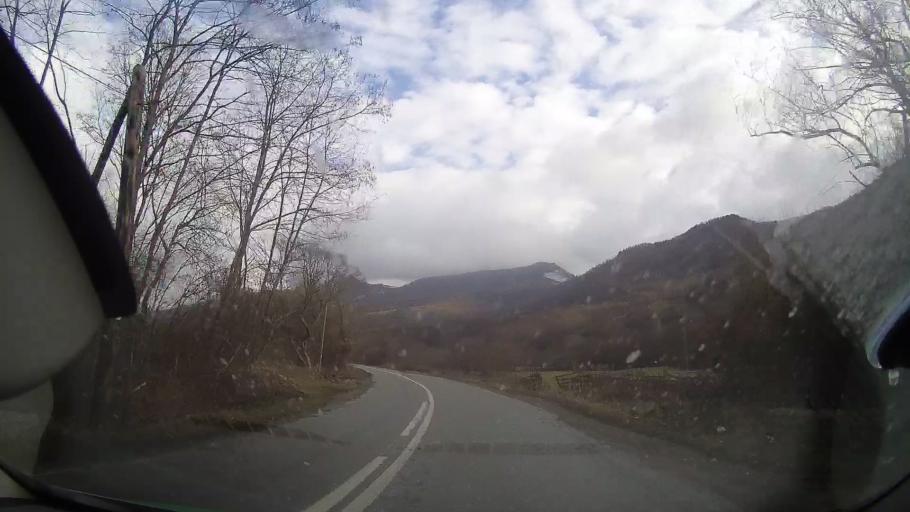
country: RO
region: Alba
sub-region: Comuna Ocolis
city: Ocolis
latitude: 46.4759
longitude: 23.5011
